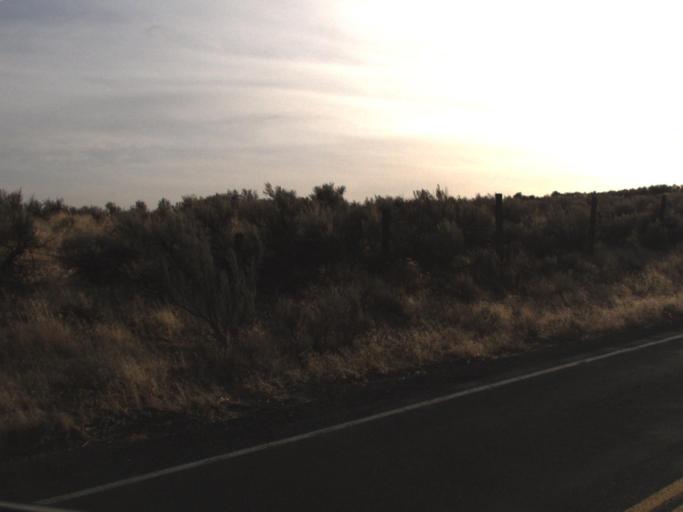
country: US
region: Washington
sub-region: Adams County
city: Ritzville
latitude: 47.3222
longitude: -118.6895
